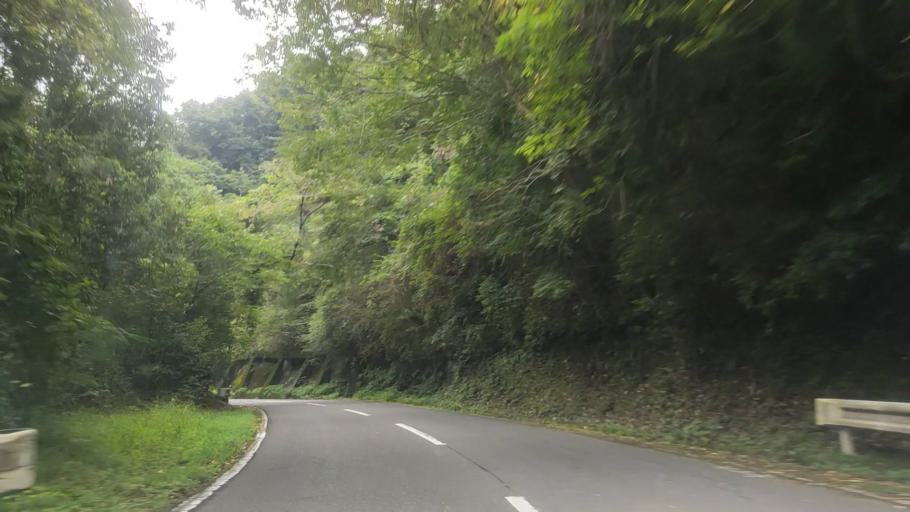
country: JP
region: Wakayama
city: Koya
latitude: 34.2554
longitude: 135.5431
